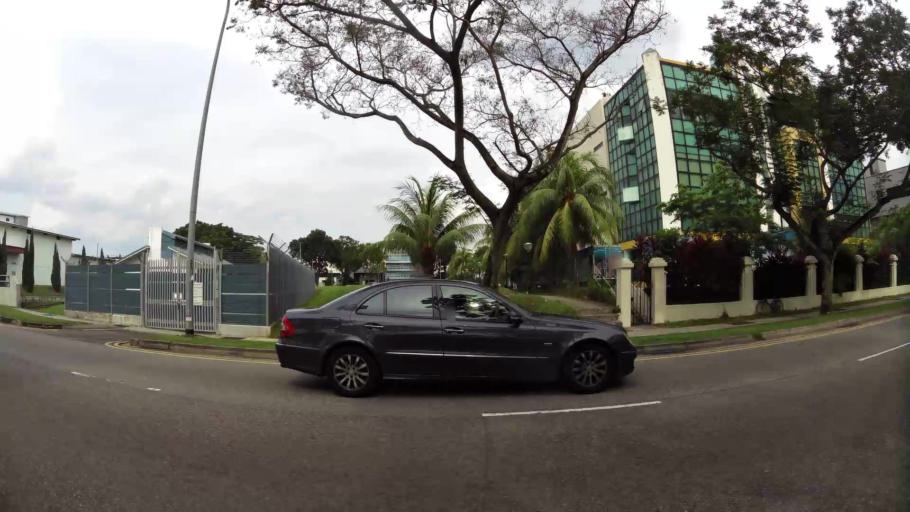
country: MY
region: Johor
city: Johor Bahru
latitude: 1.4527
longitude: 103.8019
